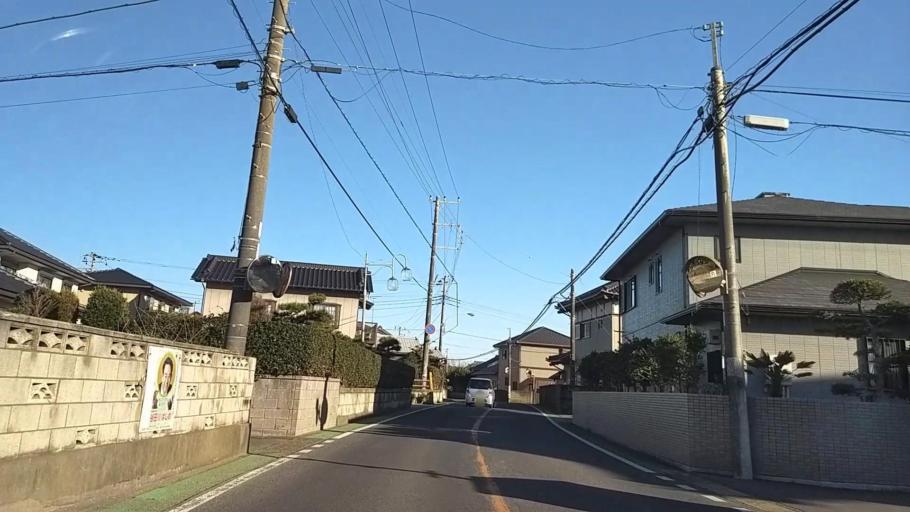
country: JP
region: Chiba
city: Asahi
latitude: 35.6943
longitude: 140.6624
